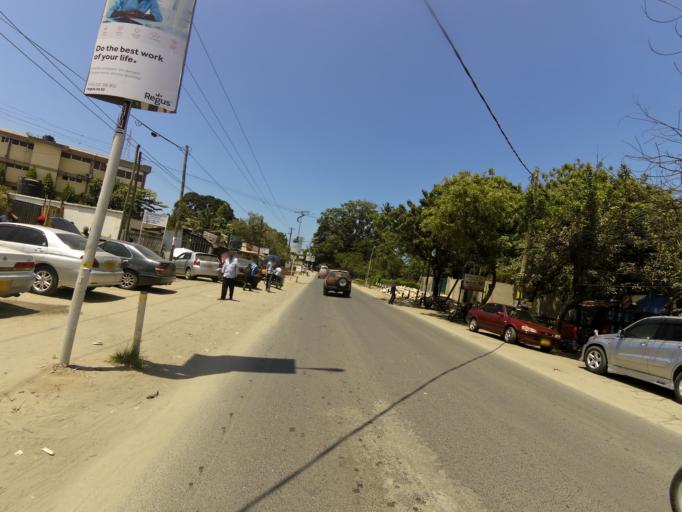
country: TZ
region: Dar es Salaam
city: Magomeni
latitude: -6.7904
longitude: 39.2708
